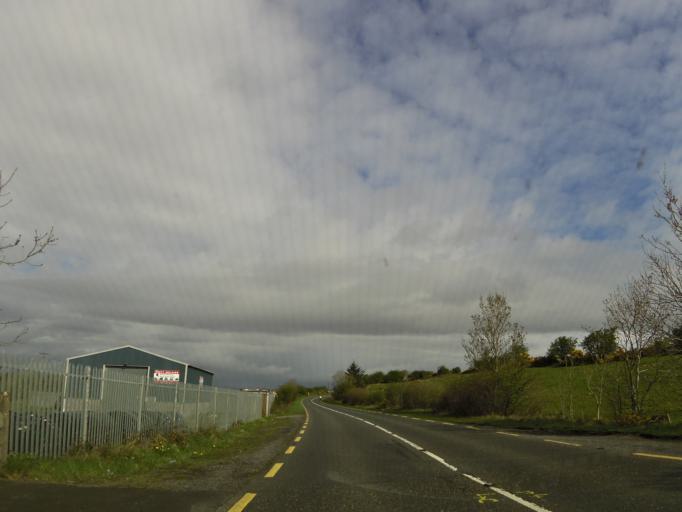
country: IE
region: Connaught
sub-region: Sligo
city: Tobercurry
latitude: 53.9458
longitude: -8.7926
